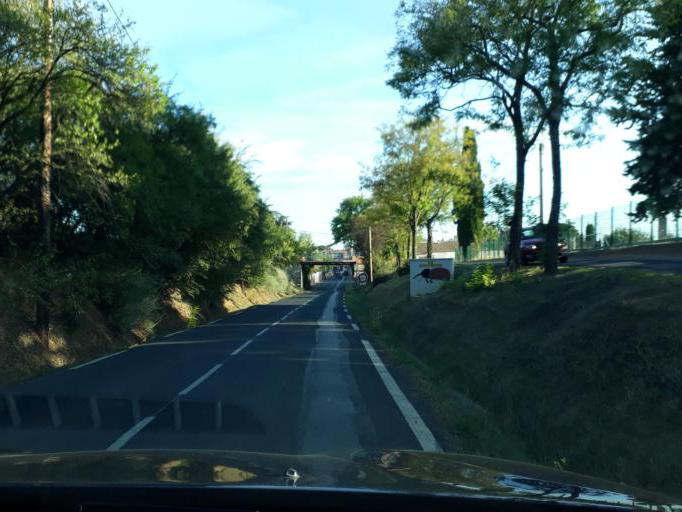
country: FR
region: Languedoc-Roussillon
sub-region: Departement de l'Herault
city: Pomerols
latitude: 43.3946
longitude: 3.4977
